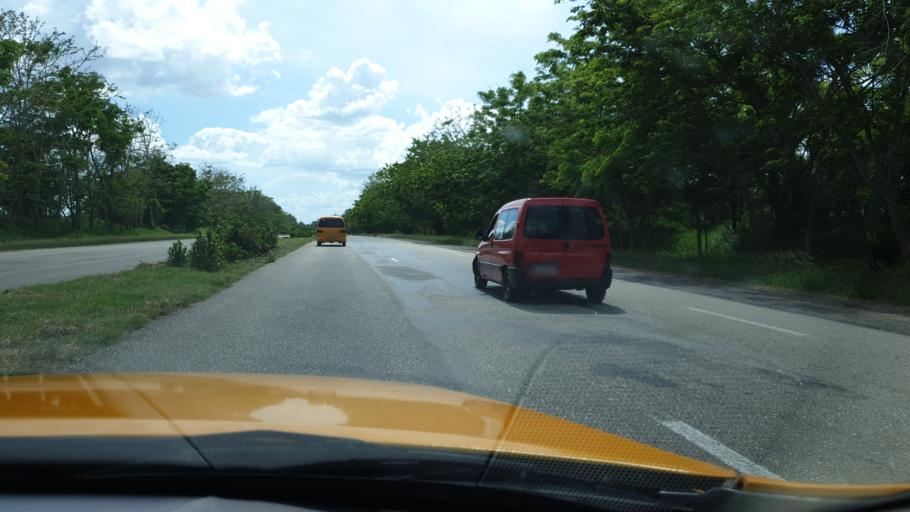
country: CU
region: Cienfuegos
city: Cruces
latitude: 22.4554
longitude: -80.3106
